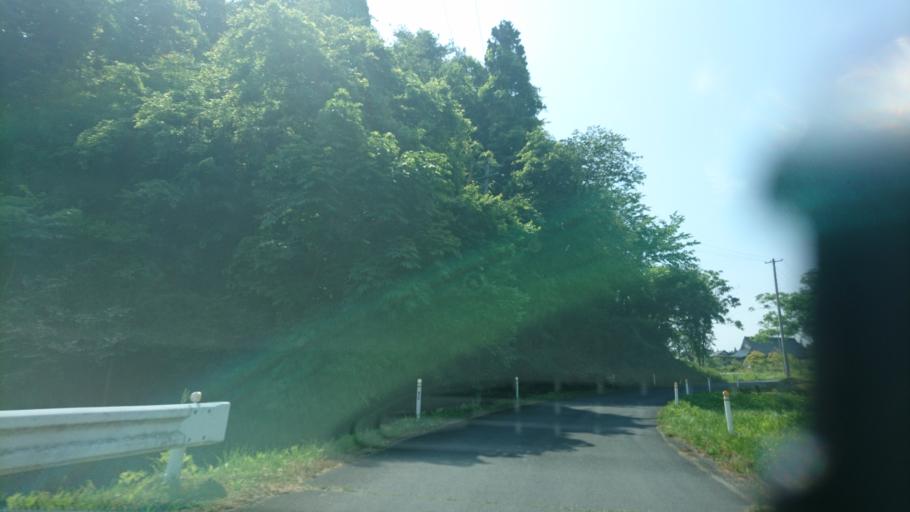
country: JP
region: Iwate
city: Ichinoseki
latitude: 38.8954
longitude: 141.3365
